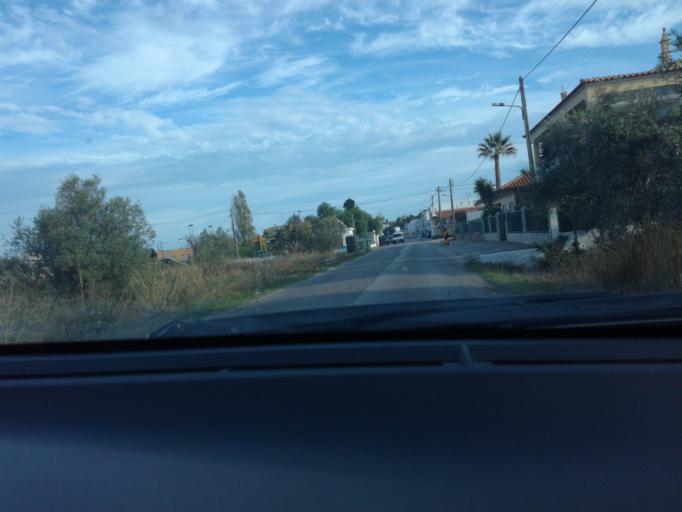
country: PT
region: Faro
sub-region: Olhao
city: Laranjeiro
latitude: 37.0643
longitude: -7.7614
